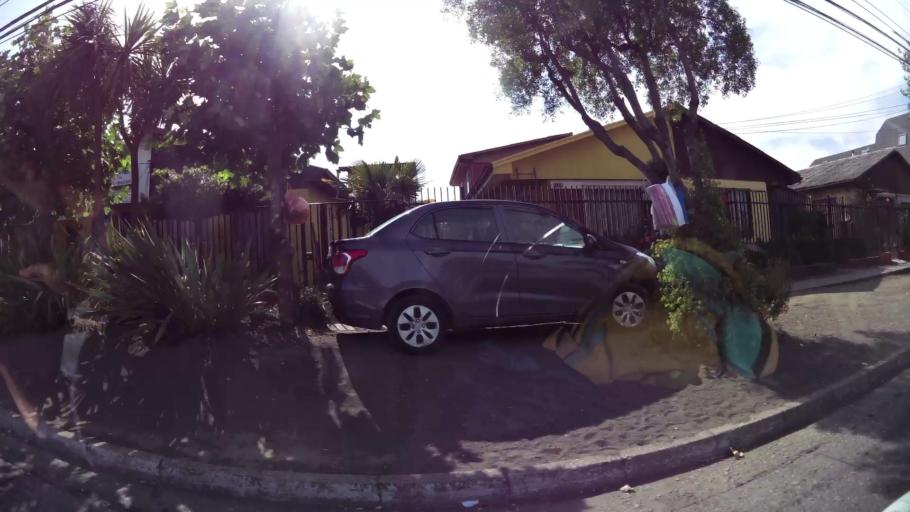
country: CL
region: Biobio
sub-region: Provincia de Concepcion
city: Talcahuano
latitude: -36.7842
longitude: -73.1016
